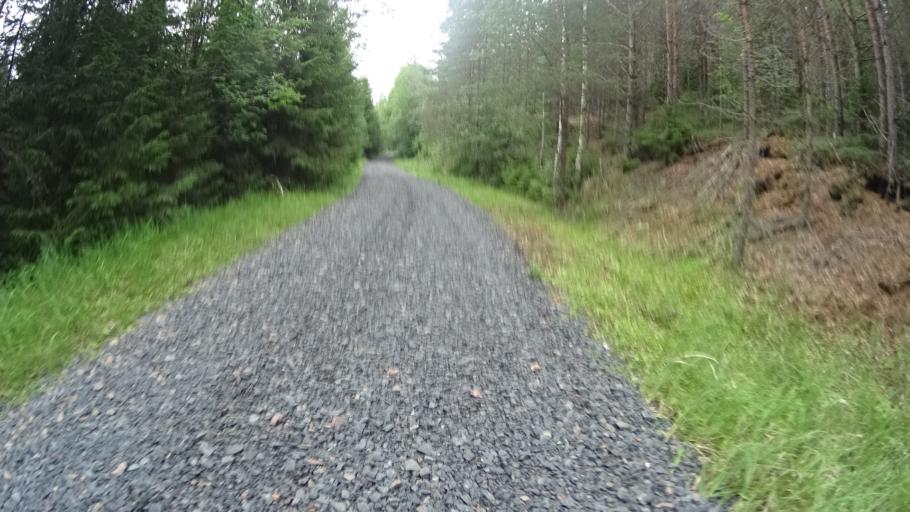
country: FI
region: Uusimaa
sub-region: Helsinki
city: Karkkila
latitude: 60.5862
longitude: 24.1552
